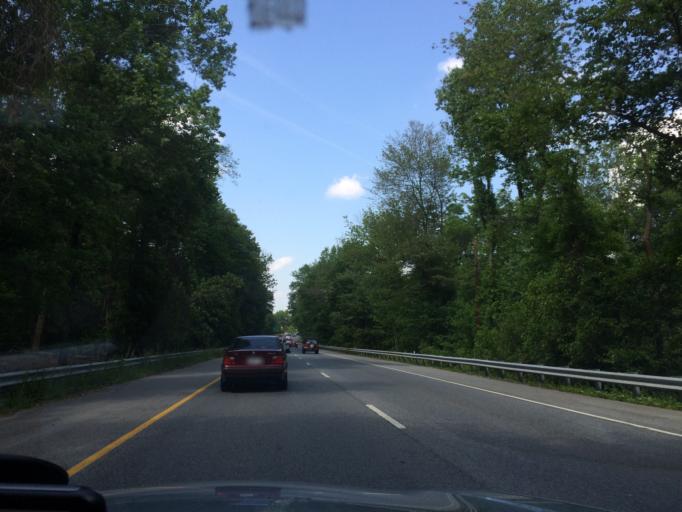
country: US
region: Maryland
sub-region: Anne Arundel County
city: Crofton
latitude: 38.9792
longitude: -76.7128
